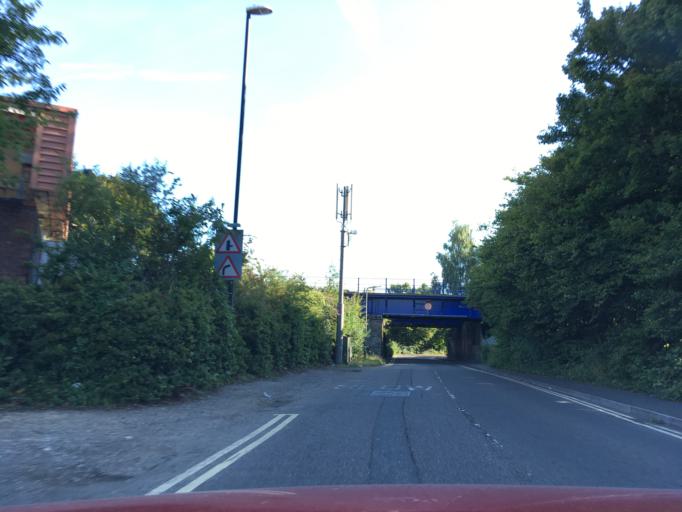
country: GB
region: England
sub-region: Bristol
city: Bristol
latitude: 51.4489
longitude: -2.5573
